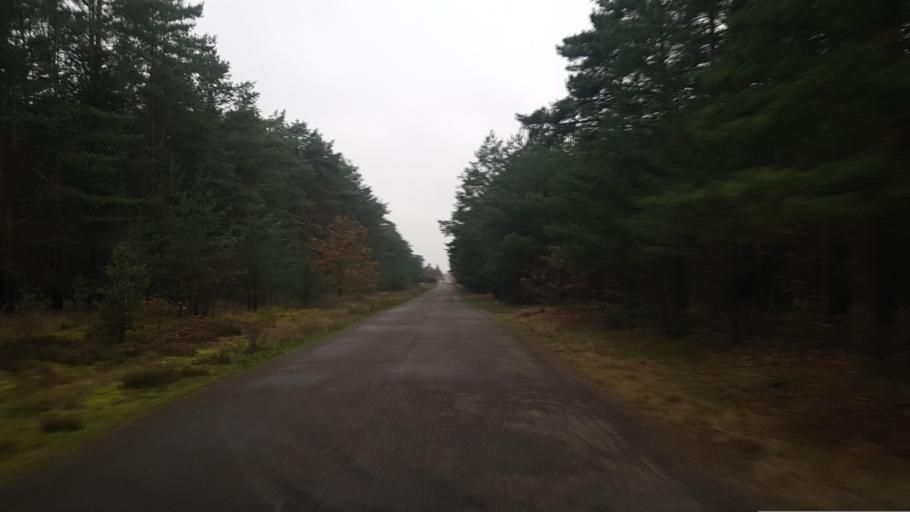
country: DE
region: Brandenburg
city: Ruhland
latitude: 51.4304
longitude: 13.8735
